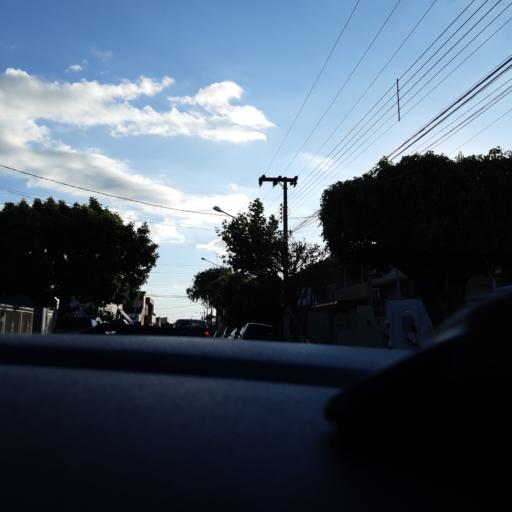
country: BR
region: Sao Paulo
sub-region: Ourinhos
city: Ourinhos
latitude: -22.9828
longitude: -49.8656
